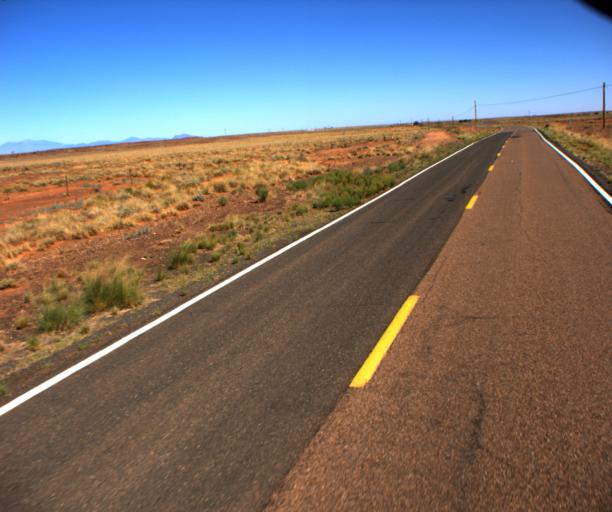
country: US
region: Arizona
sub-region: Coconino County
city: LeChee
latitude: 35.1469
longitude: -110.8949
